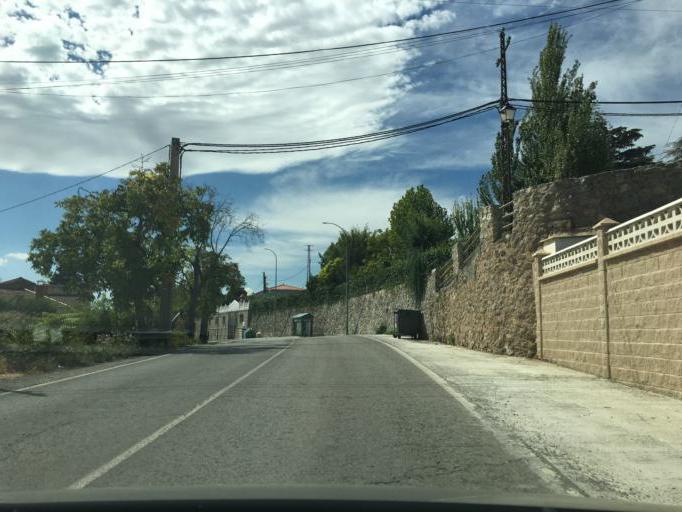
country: ES
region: Andalusia
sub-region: Provincia de Granada
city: Huetor Santillan
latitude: 37.2242
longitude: -3.5103
